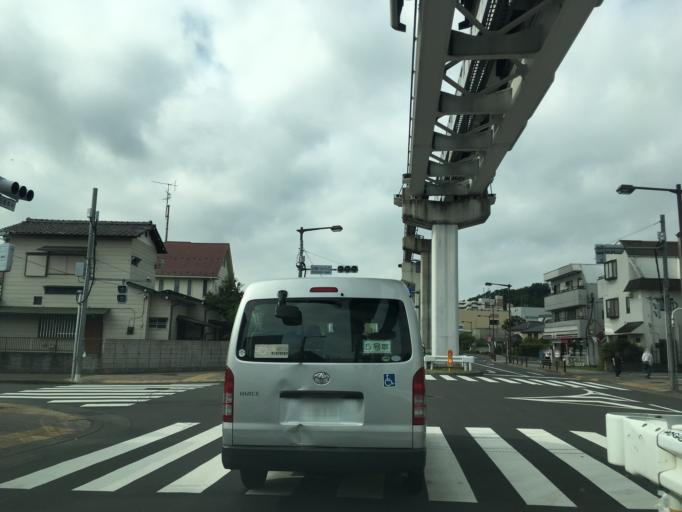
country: JP
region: Tokyo
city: Hino
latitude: 35.6637
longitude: 139.4170
